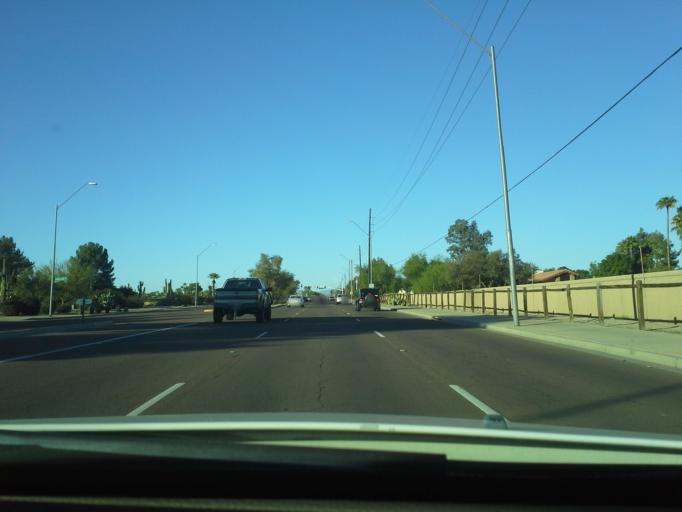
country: US
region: Arizona
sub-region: Maricopa County
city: Paradise Valley
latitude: 33.5939
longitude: -111.9258
